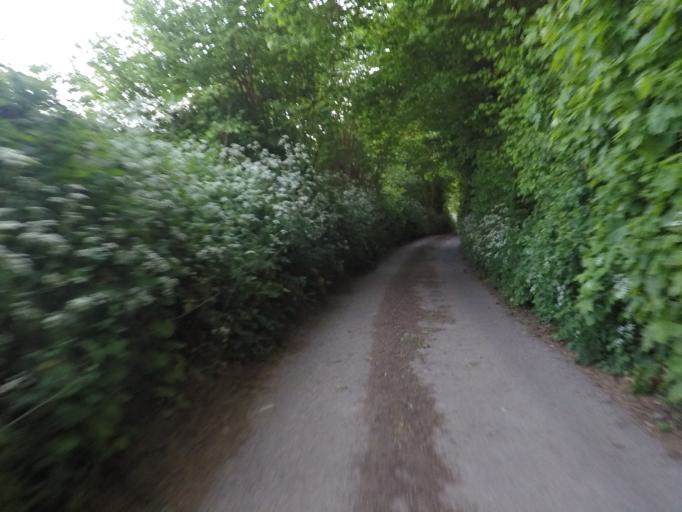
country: GB
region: England
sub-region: Oxfordshire
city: Charlbury
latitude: 51.8358
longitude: -1.5283
